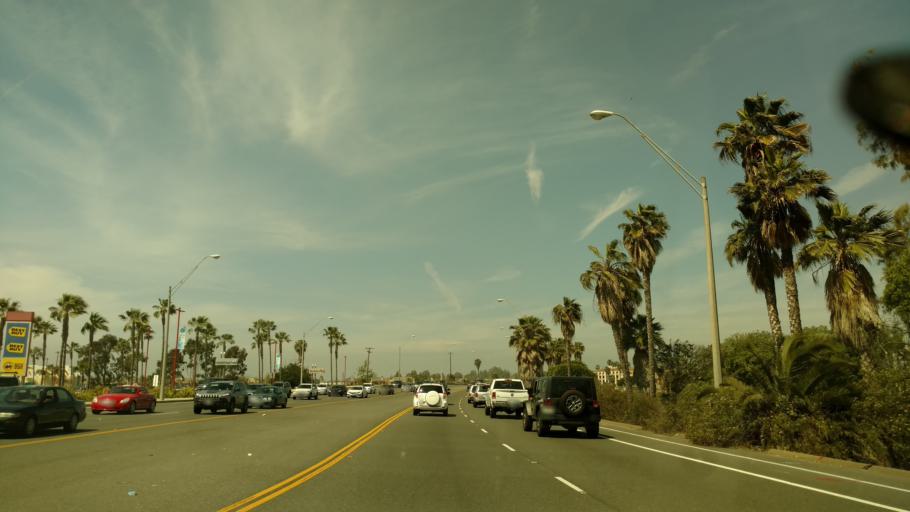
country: US
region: California
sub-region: Orange County
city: Seal Beach
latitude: 33.7611
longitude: -118.1139
